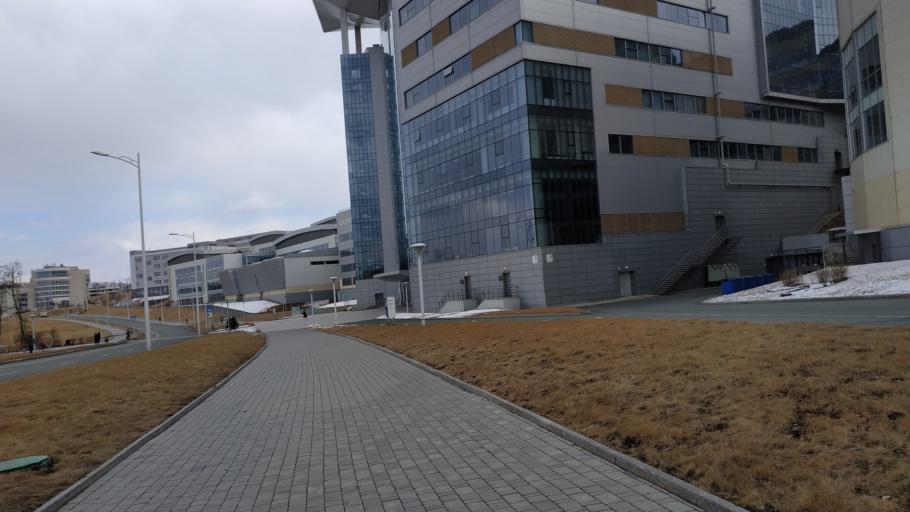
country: RU
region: Primorskiy
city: Russkiy
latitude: 43.0253
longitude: 131.8930
